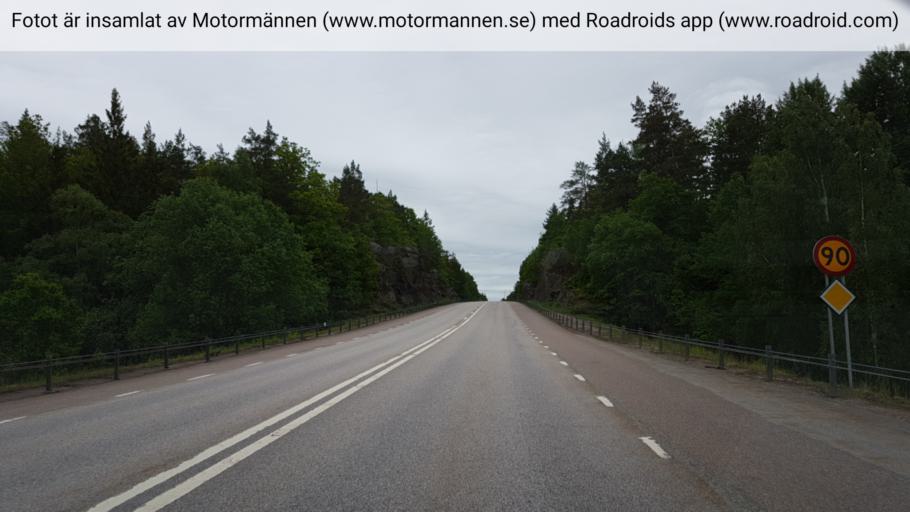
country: SE
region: Kalmar
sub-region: Vasterviks Kommun
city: Ankarsrum
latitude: 57.5451
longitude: 16.4789
